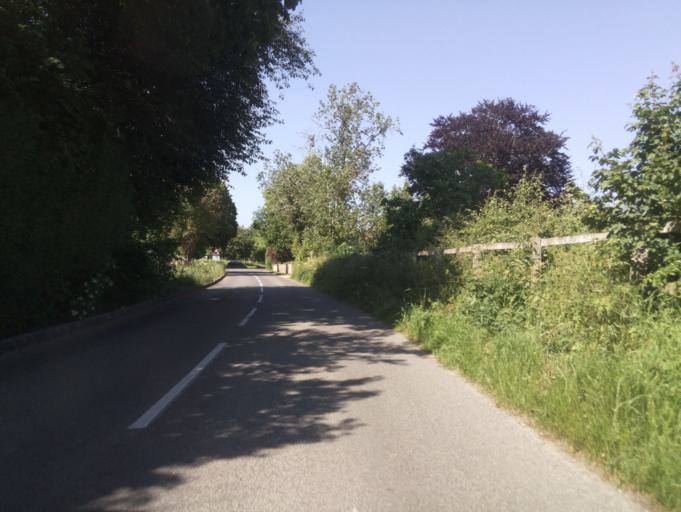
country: GB
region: England
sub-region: Hampshire
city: Abbotts Ann
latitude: 51.2328
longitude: -1.5628
